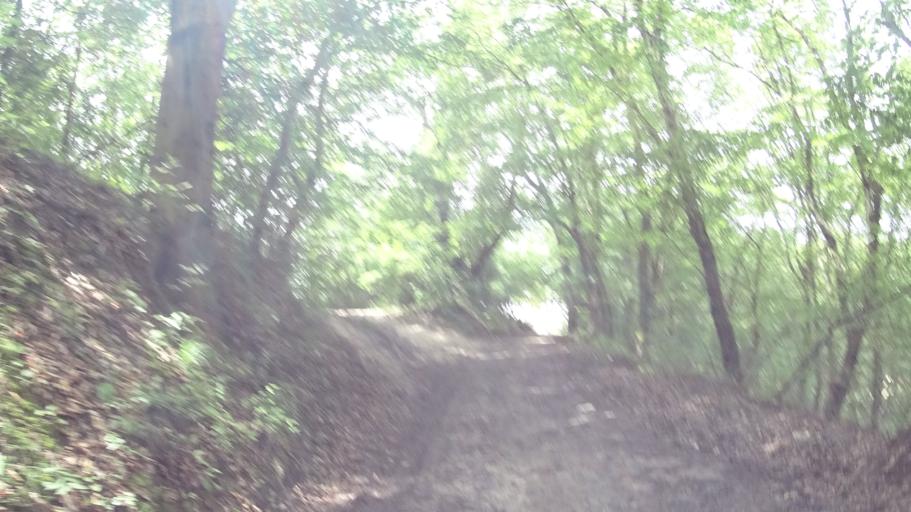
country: HU
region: Komarom-Esztergom
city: Pilismarot
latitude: 47.7992
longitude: 18.9150
